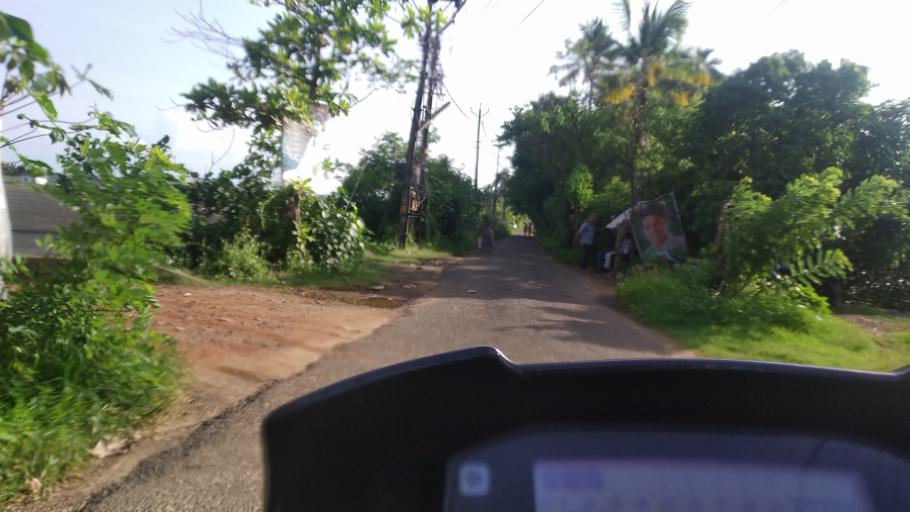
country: IN
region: Kerala
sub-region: Thrissur District
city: Kodungallur
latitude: 10.1324
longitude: 76.1904
